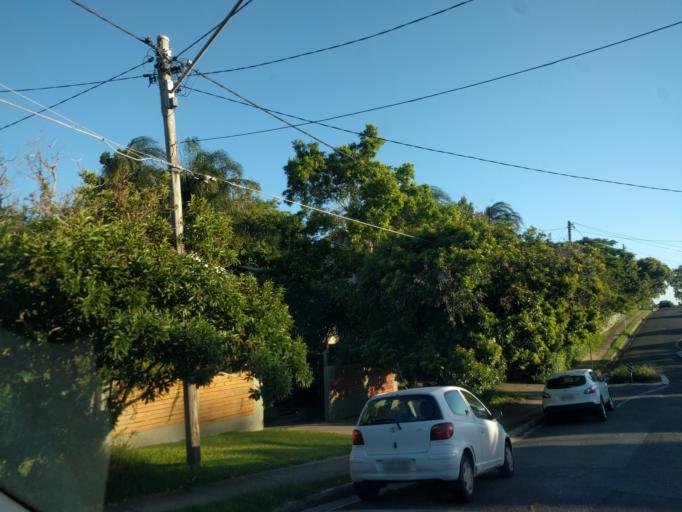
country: AU
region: Queensland
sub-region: Brisbane
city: Annerley
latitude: -27.5031
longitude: 153.0292
